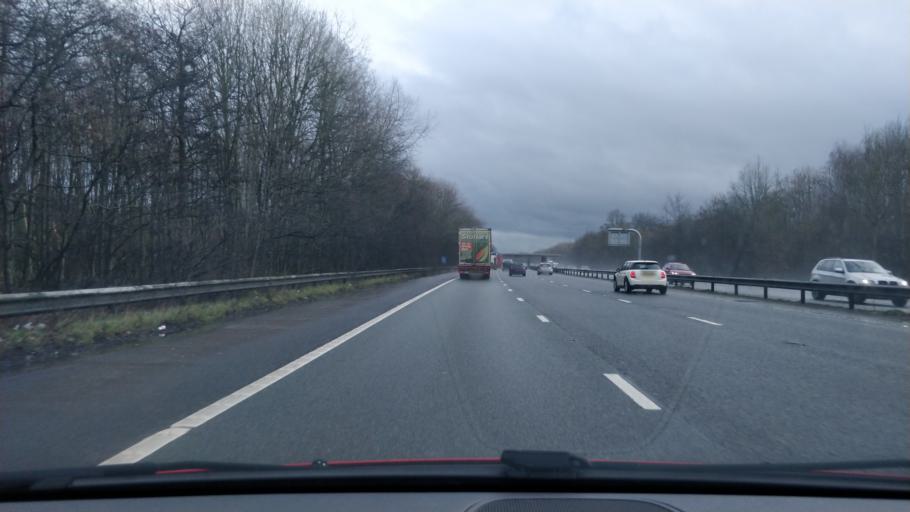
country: GB
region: England
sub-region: Knowsley
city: Knowsley
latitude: 53.4447
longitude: -2.8592
